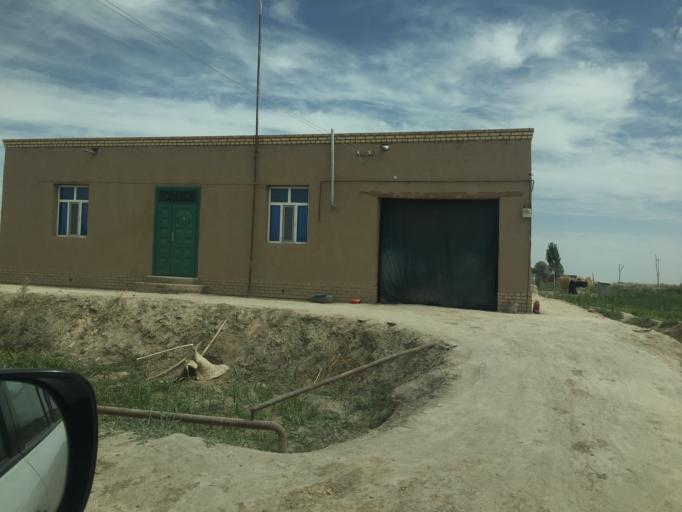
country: TM
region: Dasoguz
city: Tagta
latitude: 41.6002
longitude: 59.8583
